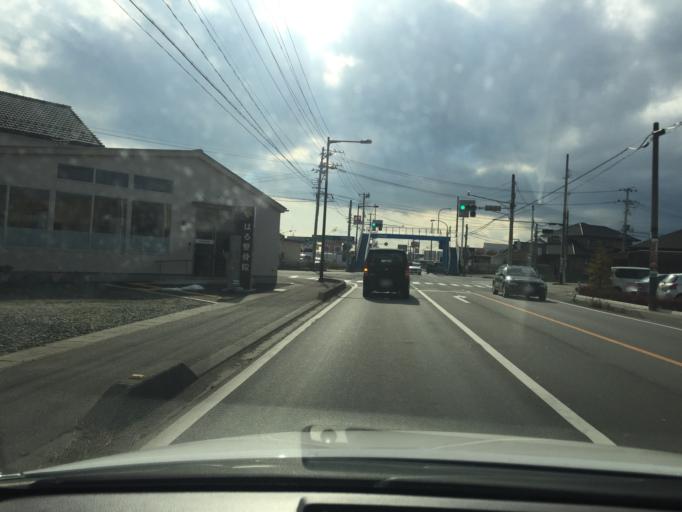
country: JP
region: Fukushima
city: Iwaki
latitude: 36.9546
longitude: 140.8667
